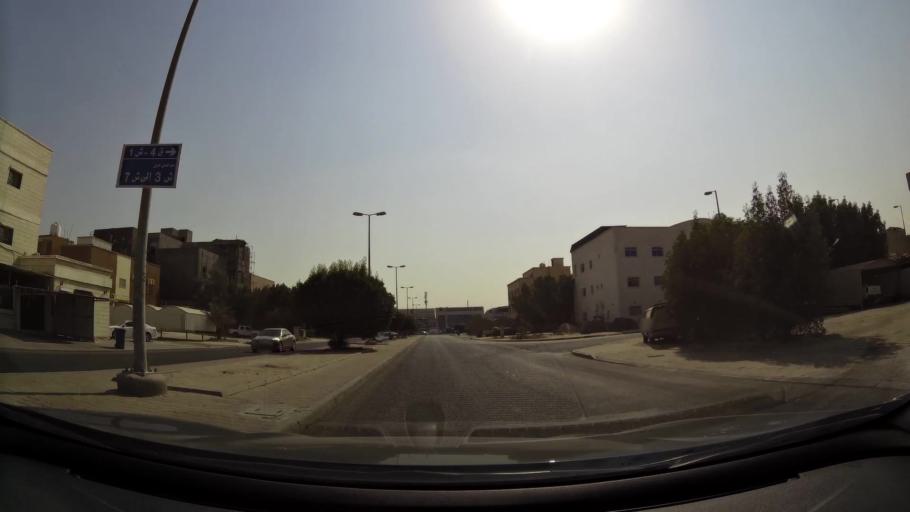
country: KW
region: Al Ahmadi
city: Al Fahahil
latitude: 29.0755
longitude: 48.1175
